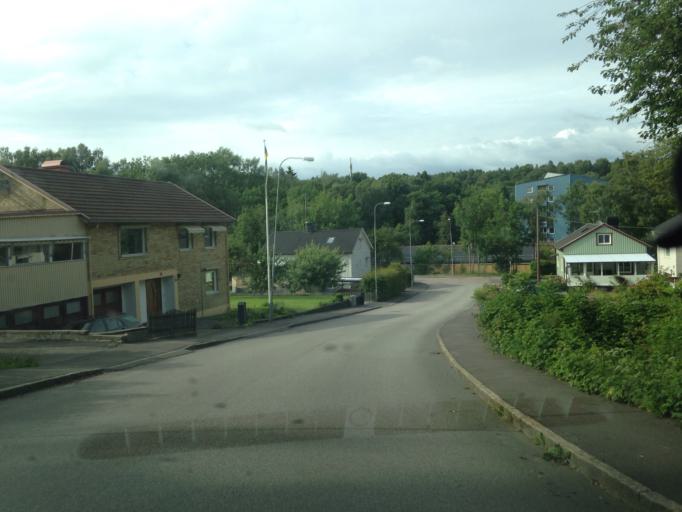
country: SE
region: Vaestra Goetaland
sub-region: Goteborg
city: Goeteborg
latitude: 57.7521
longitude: 11.9713
